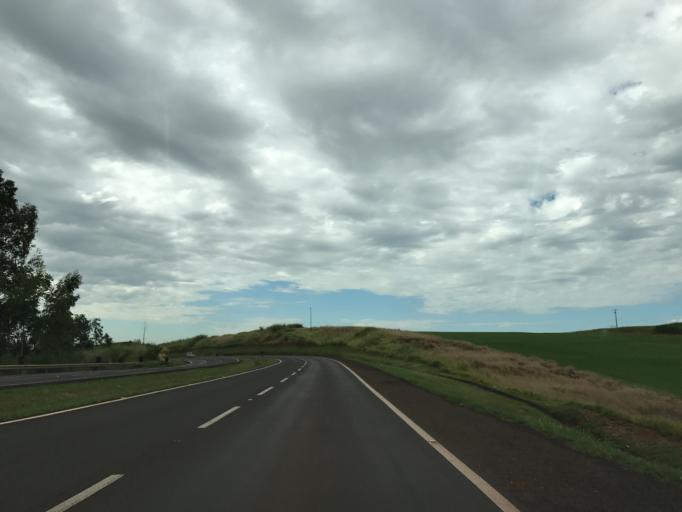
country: BR
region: Parana
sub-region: Rolandia
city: Rolandia
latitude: -23.3404
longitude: -51.3570
